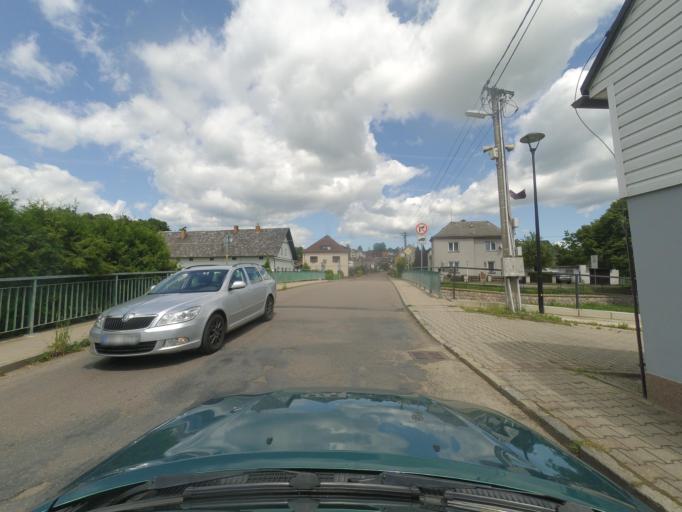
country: CZ
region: Pardubicky
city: Zamberk
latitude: 50.0890
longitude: 16.4675
